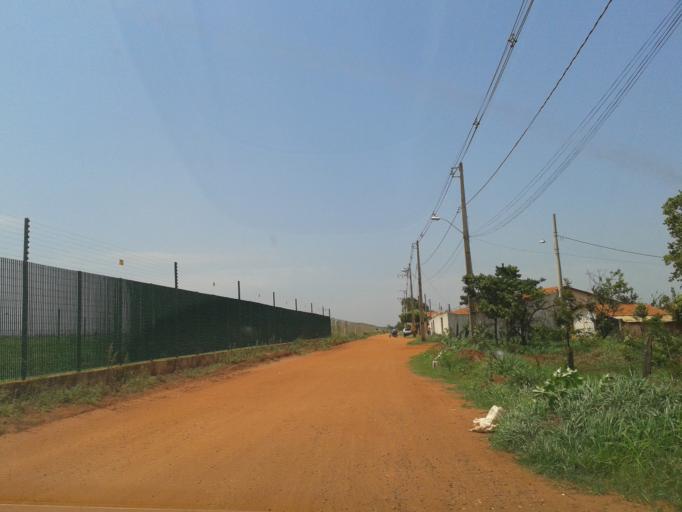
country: BR
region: Minas Gerais
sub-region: Ituiutaba
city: Ituiutaba
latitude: -18.9897
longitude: -49.4335
